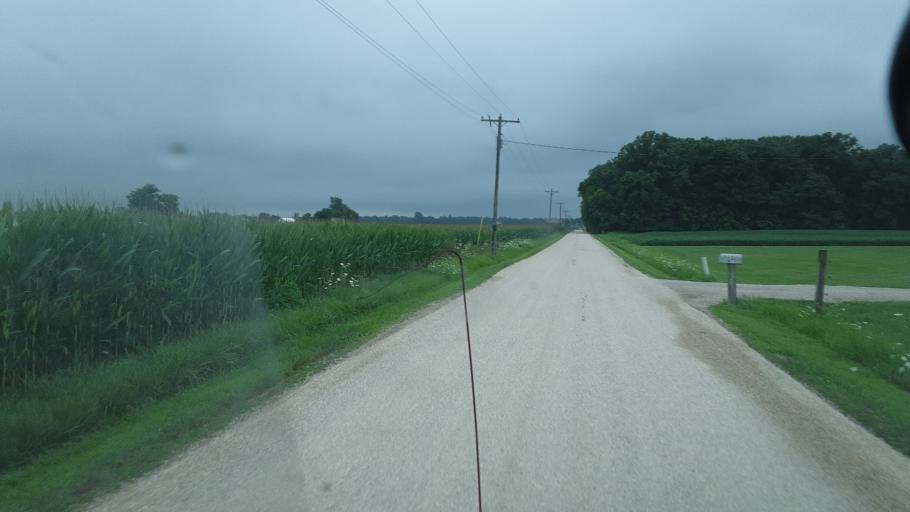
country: US
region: Indiana
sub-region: Adams County
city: Berne
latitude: 40.6419
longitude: -85.0059
